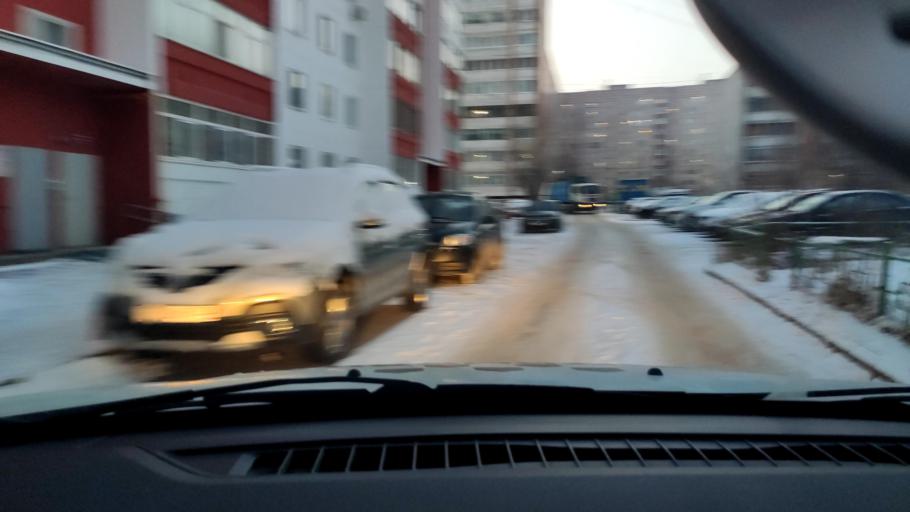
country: RU
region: Perm
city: Kondratovo
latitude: 58.0254
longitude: 56.0195
